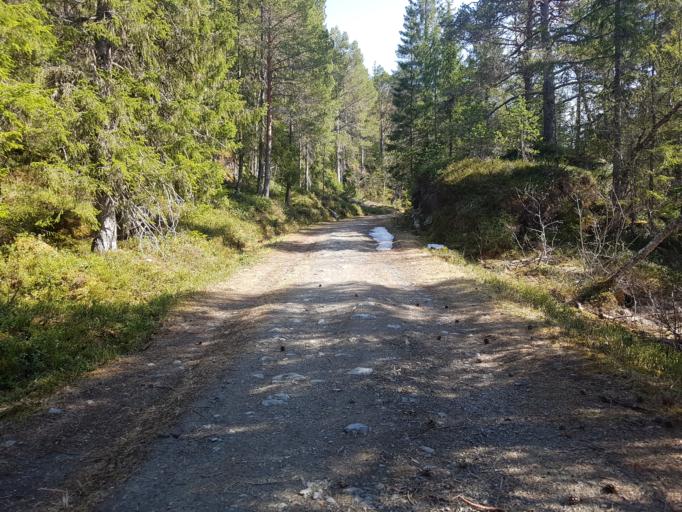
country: NO
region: Sor-Trondelag
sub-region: Trondheim
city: Trondheim
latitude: 63.4335
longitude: 10.2922
